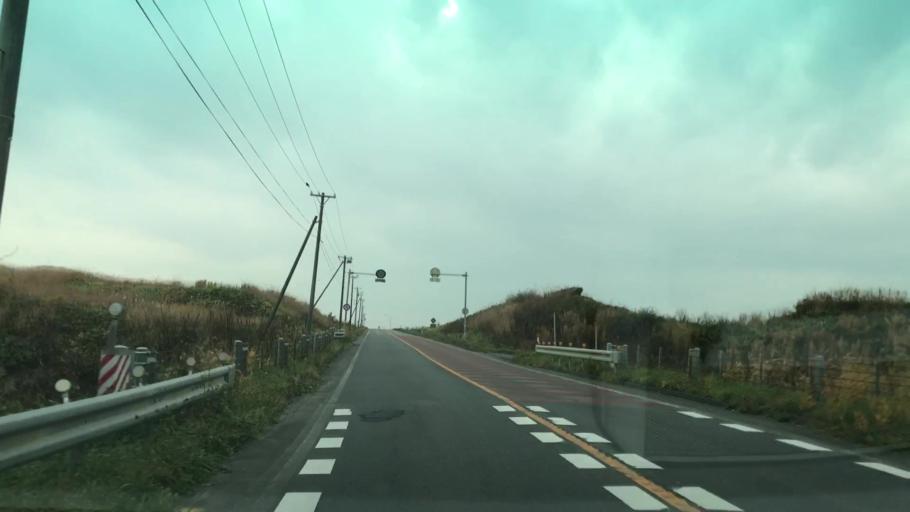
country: JP
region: Hokkaido
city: Ishikari
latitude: 43.3533
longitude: 141.4278
